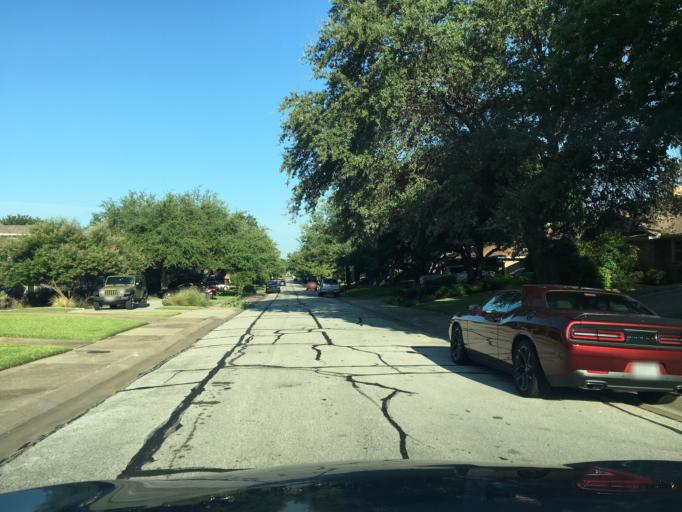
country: US
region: Texas
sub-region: Dallas County
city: Addison
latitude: 32.9667
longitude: -96.8577
